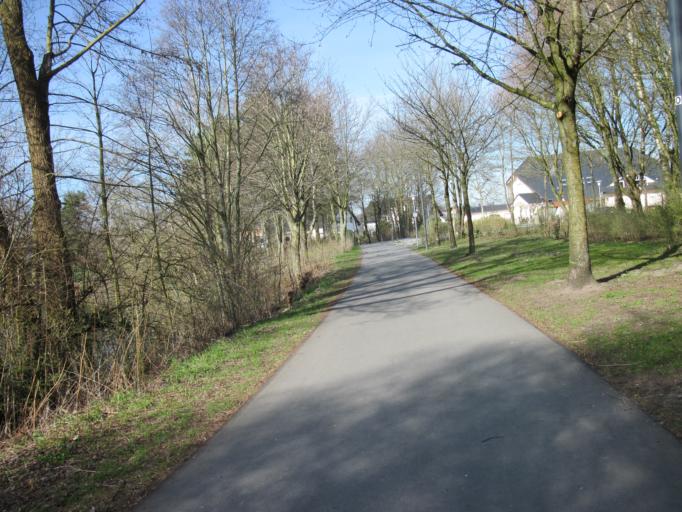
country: DE
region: North Rhine-Westphalia
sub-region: Regierungsbezirk Detmold
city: Schlangen
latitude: 51.7942
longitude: 8.8392
